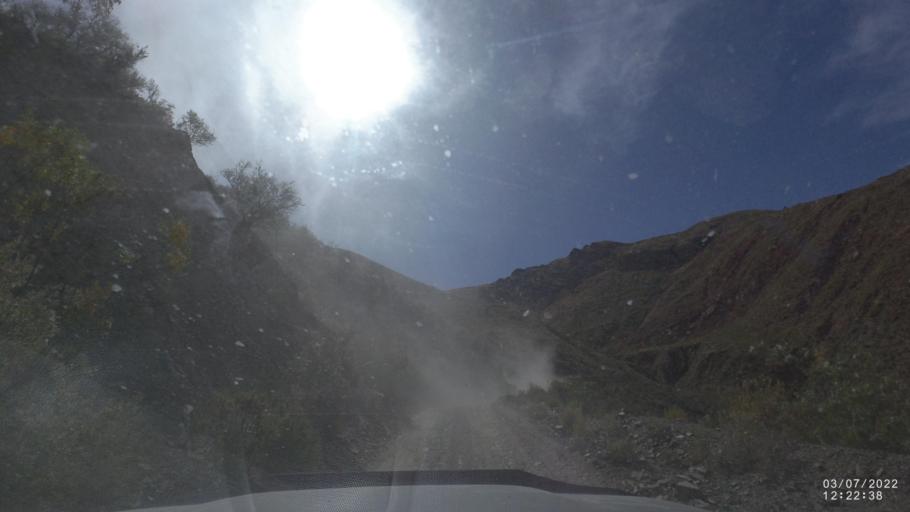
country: BO
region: Cochabamba
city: Irpa Irpa
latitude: -17.8156
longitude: -66.6188
